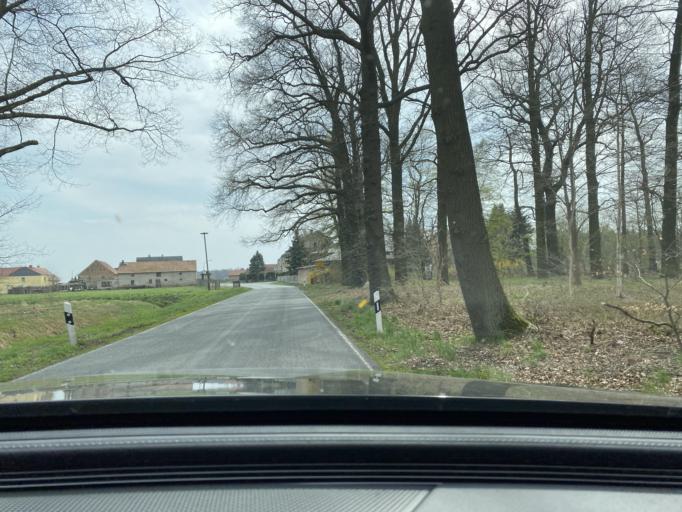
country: DE
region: Saxony
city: Konigswartha
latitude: 51.3183
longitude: 14.3079
